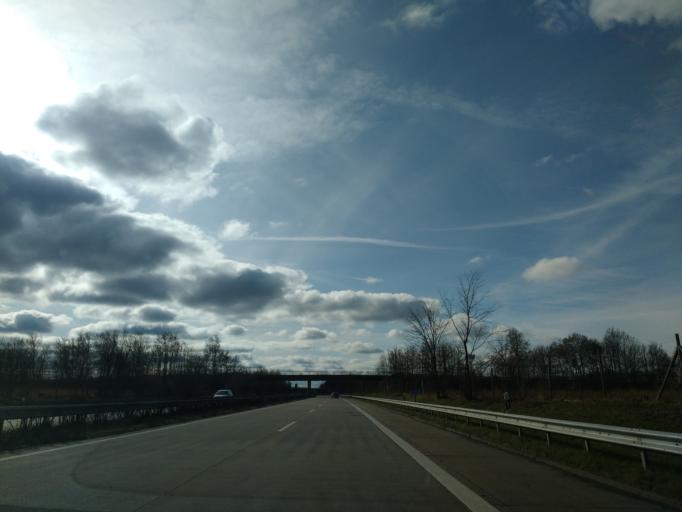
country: DE
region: Lower Saxony
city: Midlum
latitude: 53.6834
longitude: 8.6587
